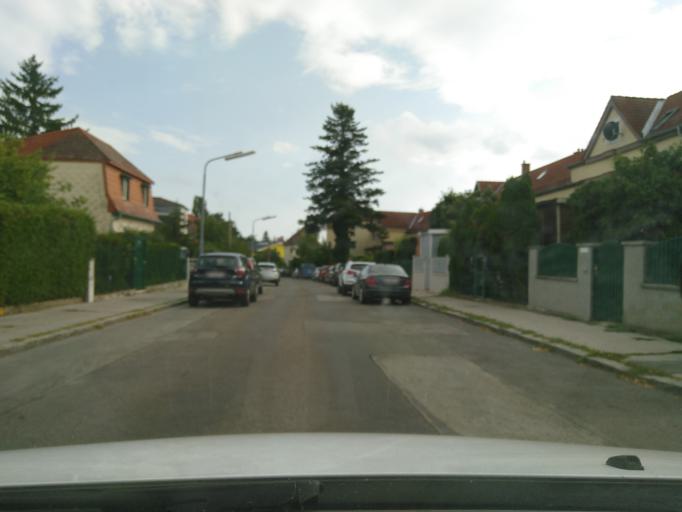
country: AT
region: Vienna
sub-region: Wien Stadt
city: Vienna
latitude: 48.2020
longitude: 16.2889
